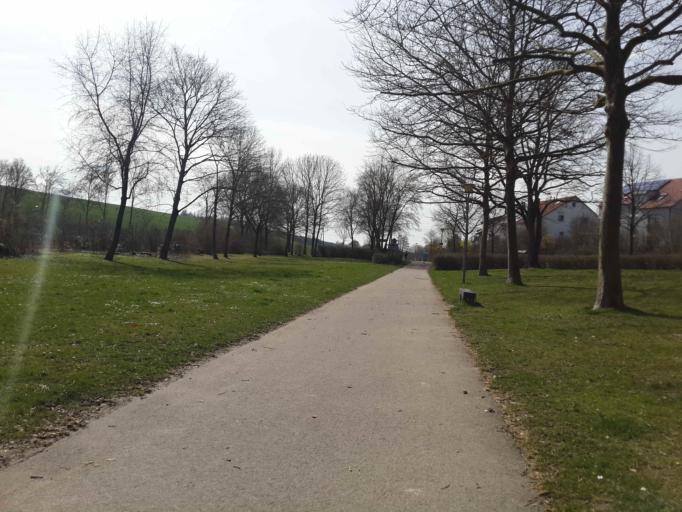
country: DE
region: Baden-Wuerttemberg
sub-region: Regierungsbezirk Stuttgart
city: Nordheim
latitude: 49.1031
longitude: 9.1282
